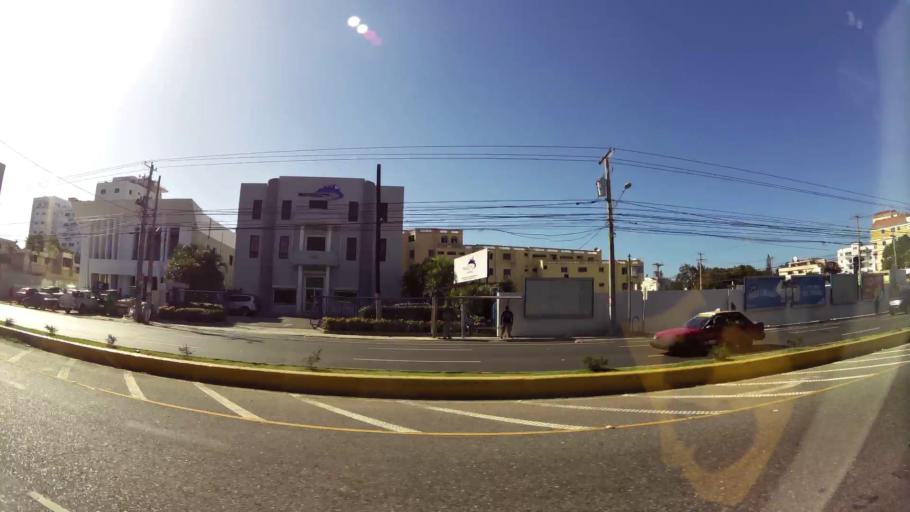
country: DO
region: Nacional
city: Bella Vista
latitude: 18.4499
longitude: -69.9680
